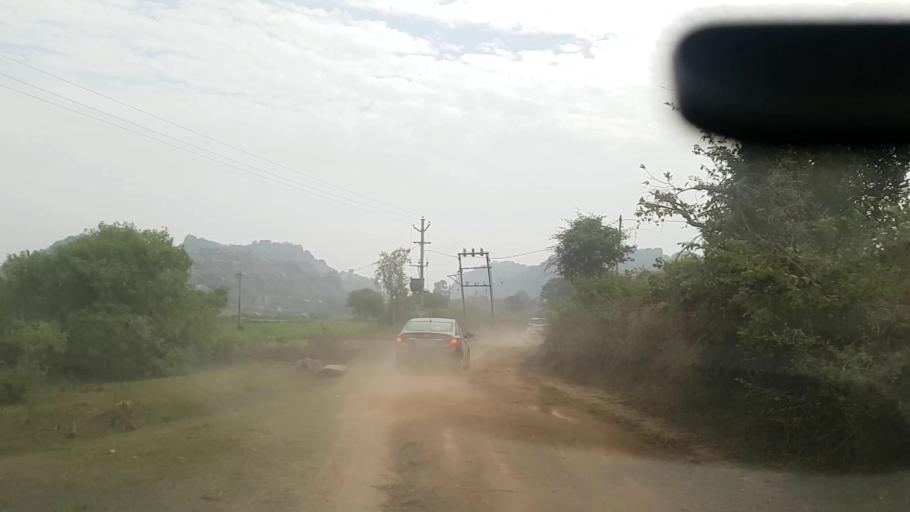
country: IN
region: Telangana
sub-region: Rangareddi
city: Lal Bahadur Nagar
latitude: 17.1810
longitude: 78.7887
